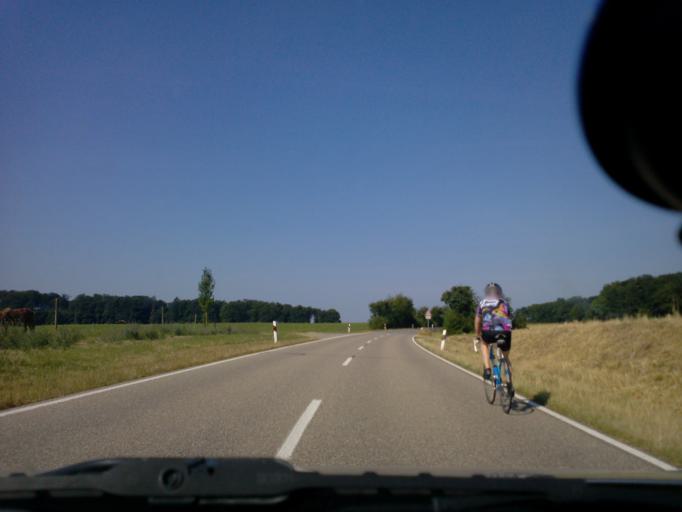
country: DE
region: Baden-Wuerttemberg
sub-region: Karlsruhe Region
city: Gondelsheim
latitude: 49.0597
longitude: 8.6194
